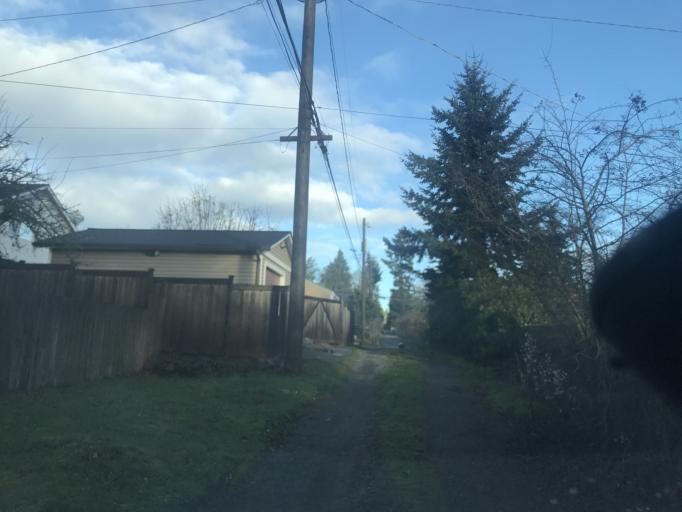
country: US
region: Washington
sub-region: King County
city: White Center
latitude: 47.5238
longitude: -122.3733
